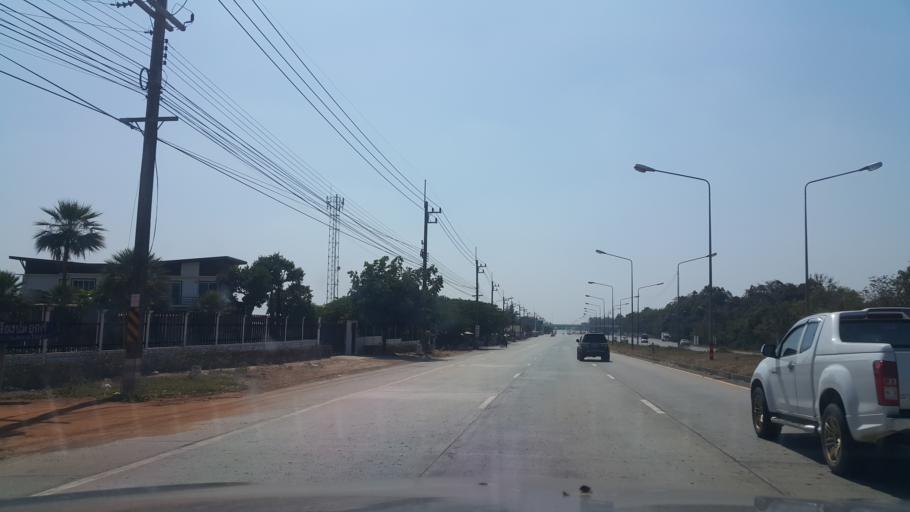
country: TH
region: Changwat Udon Thani
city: Non Sa-at
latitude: 16.8666
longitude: 102.8684
